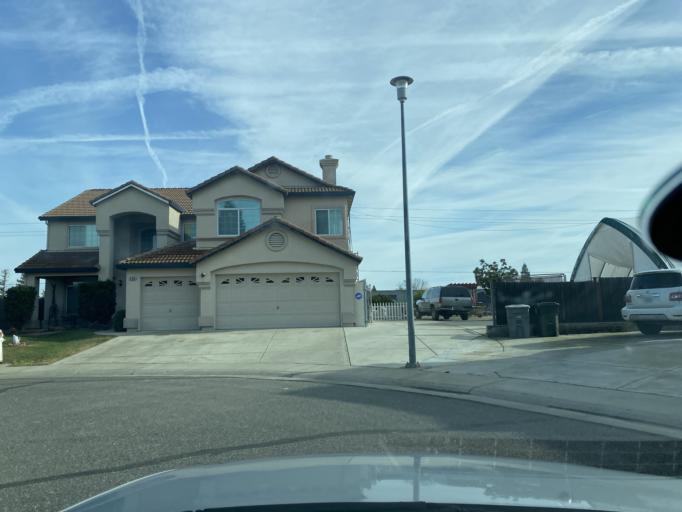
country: US
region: California
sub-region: Sacramento County
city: Elk Grove
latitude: 38.4410
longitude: -121.3774
